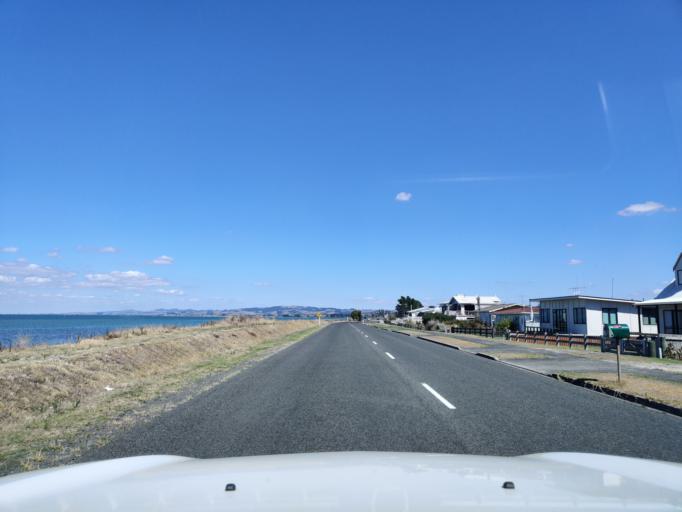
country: NZ
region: Waikato
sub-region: Thames-Coromandel District
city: Thames
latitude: -37.1072
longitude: 175.2991
